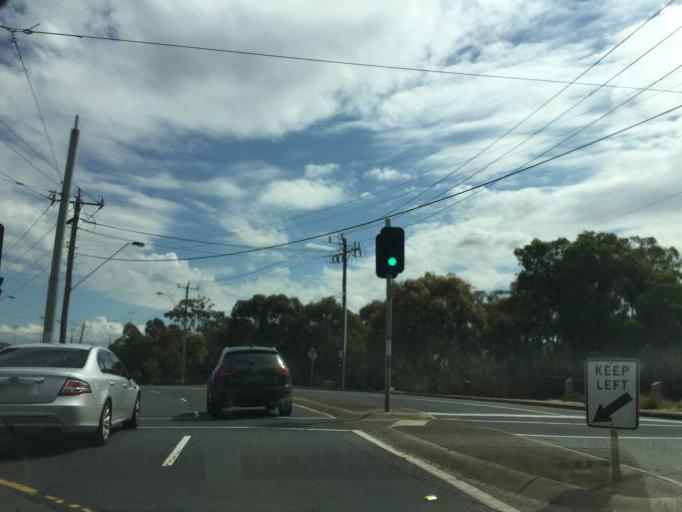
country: AU
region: Victoria
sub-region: Maribyrnong
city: Maribyrnong
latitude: -37.7802
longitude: 144.8916
